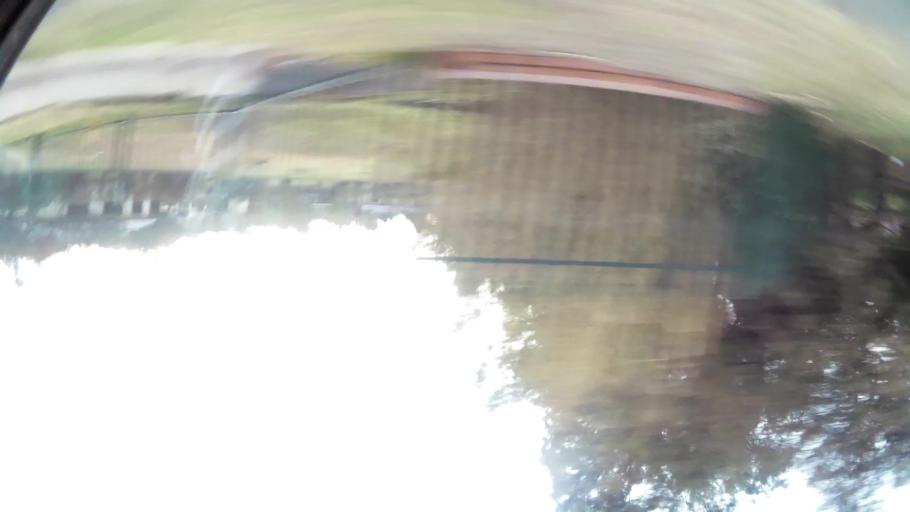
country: ZA
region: Gauteng
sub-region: City of Johannesburg Metropolitan Municipality
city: Midrand
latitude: -25.9777
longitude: 28.0758
